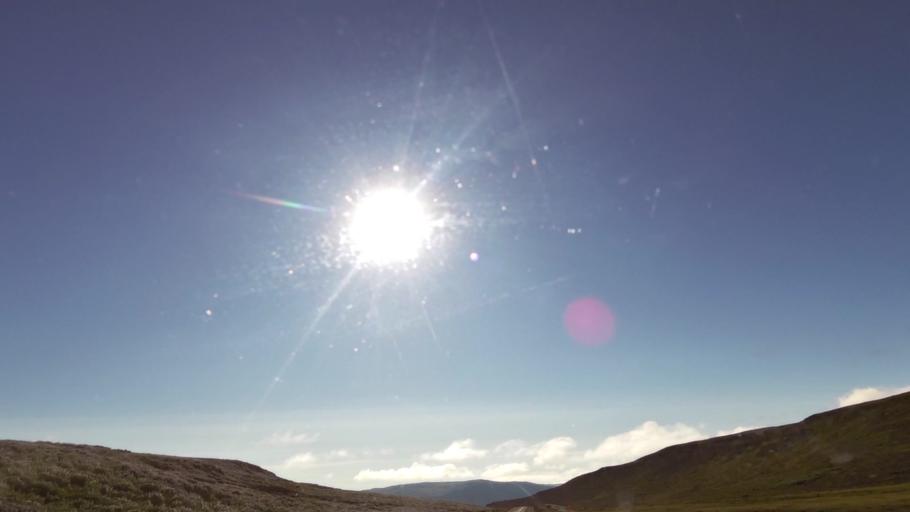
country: IS
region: West
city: Olafsvik
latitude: 65.5381
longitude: -23.8243
